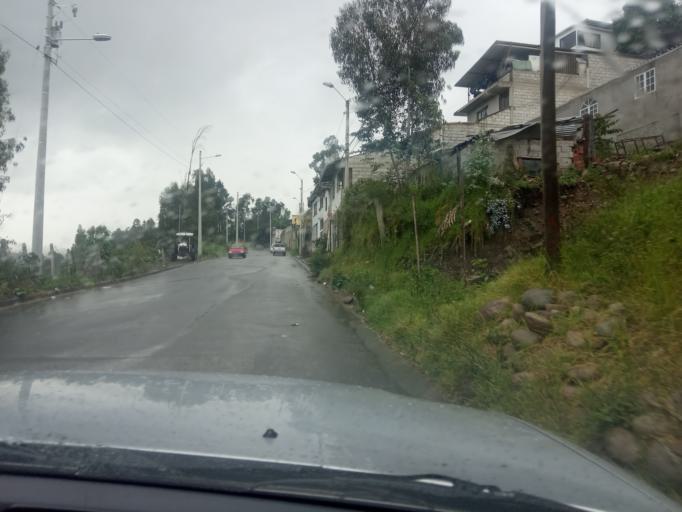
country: EC
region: Azuay
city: Llacao
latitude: -2.8631
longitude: -78.9396
